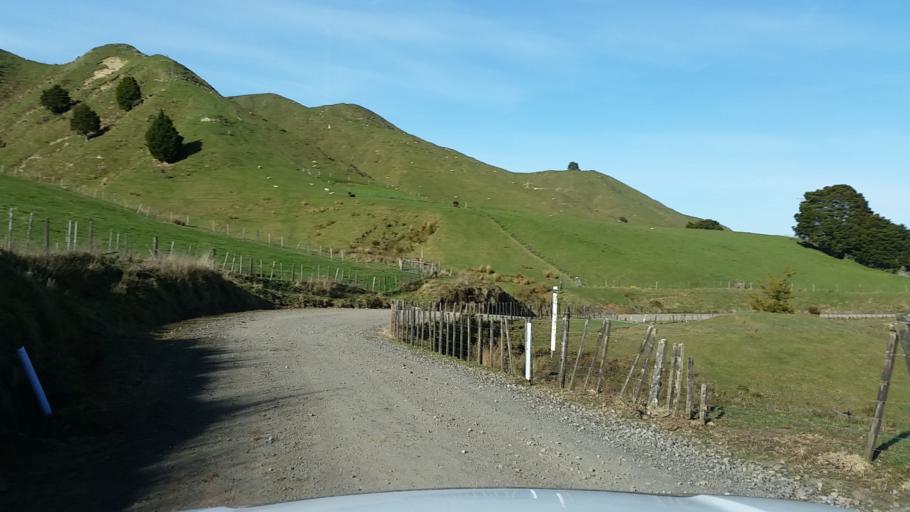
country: NZ
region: Taranaki
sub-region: South Taranaki District
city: Eltham
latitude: -39.3130
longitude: 174.5356
